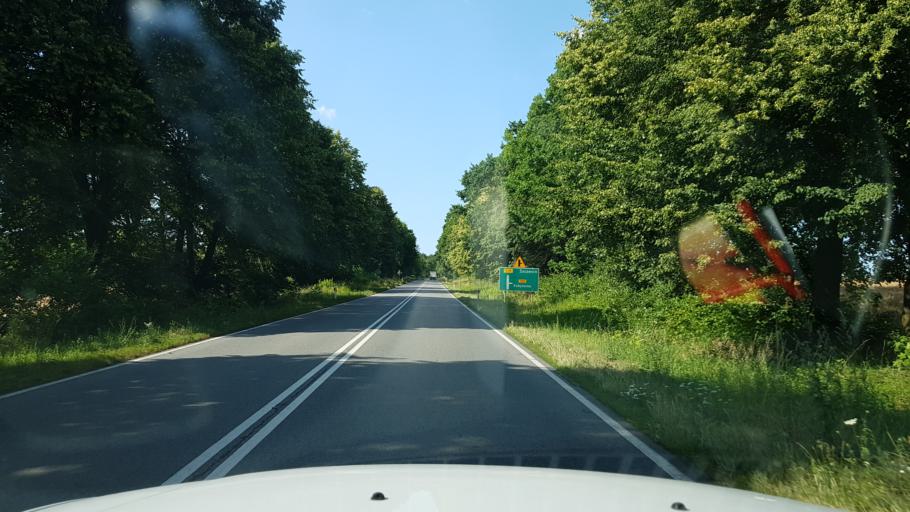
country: PL
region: West Pomeranian Voivodeship
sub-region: Powiat gryfinski
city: Stare Czarnowo
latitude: 53.3030
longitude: 14.7933
